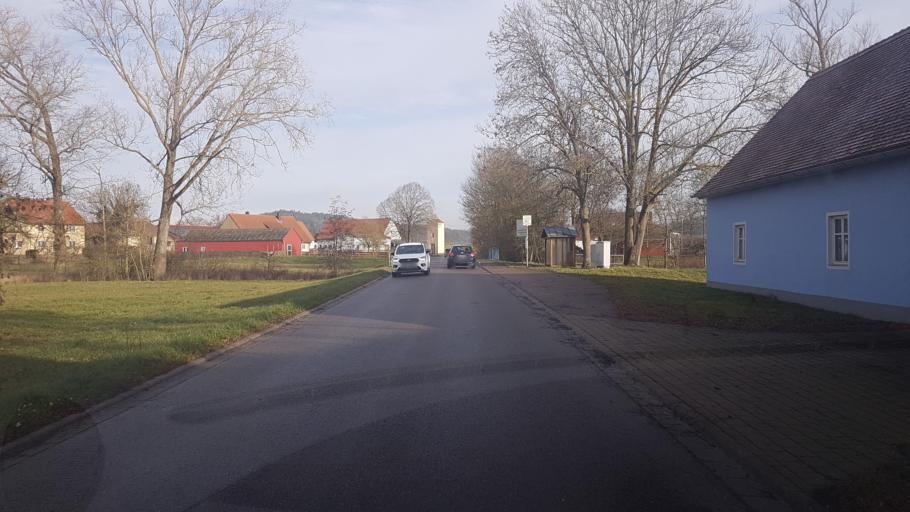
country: DE
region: Bavaria
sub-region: Regierungsbezirk Mittelfranken
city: Dombuhl
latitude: 49.2264
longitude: 10.2425
